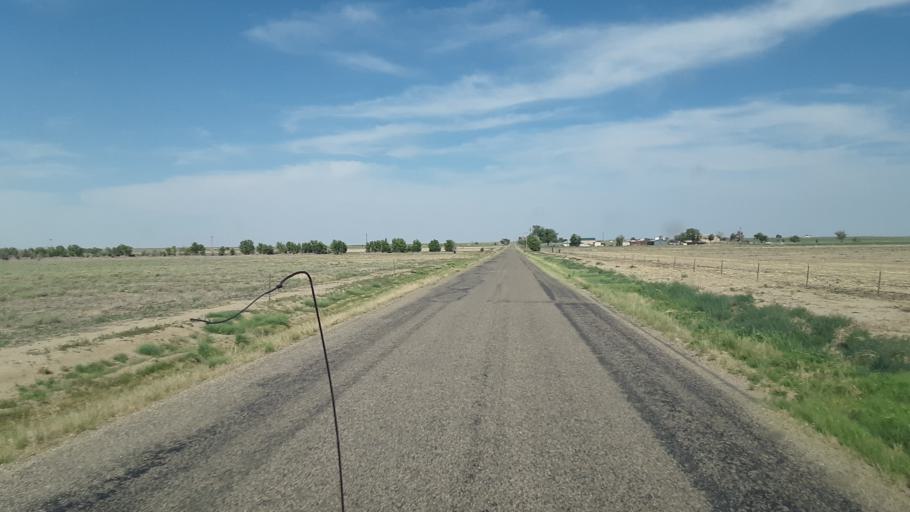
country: US
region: Colorado
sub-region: Otero County
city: Fowler
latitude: 38.1632
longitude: -103.8982
